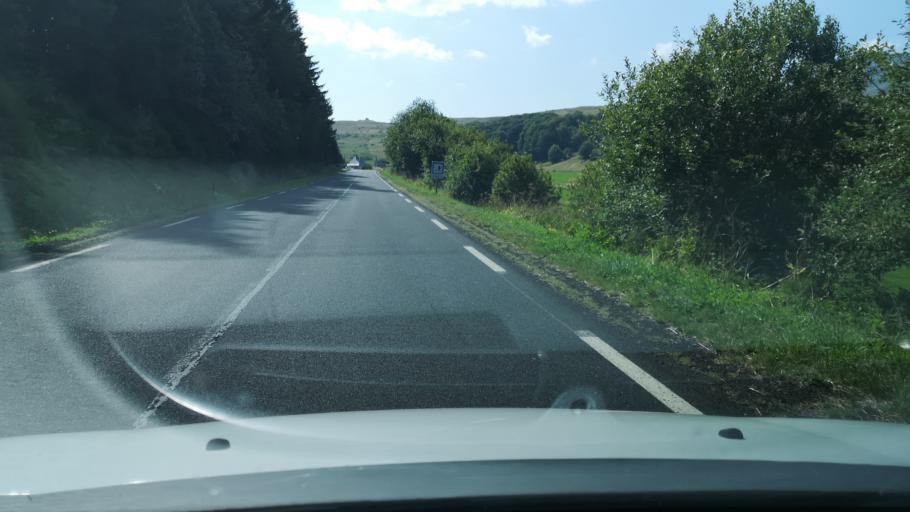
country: FR
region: Auvergne
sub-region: Departement du Puy-de-Dome
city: Mont-Dore
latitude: 45.4935
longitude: 2.8647
